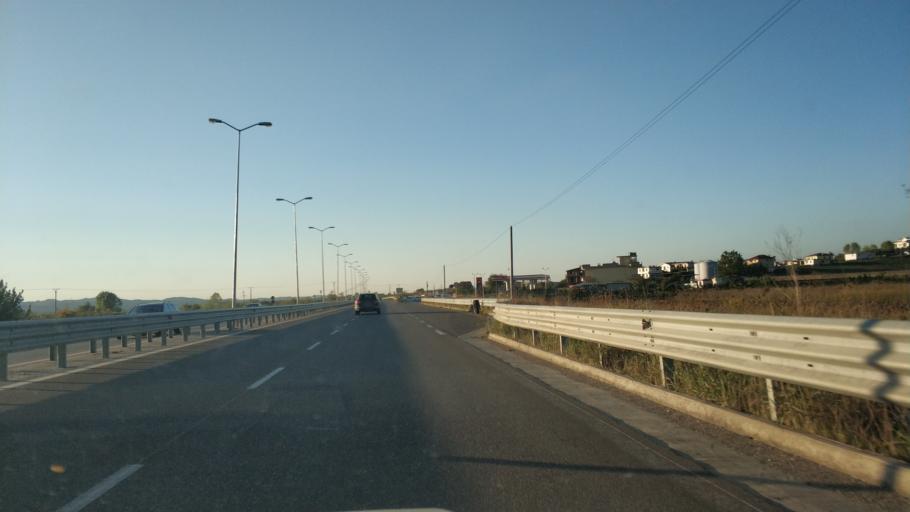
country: AL
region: Tirane
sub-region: Rrethi i Kavajes
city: Gose e Madhe
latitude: 41.0822
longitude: 19.6209
